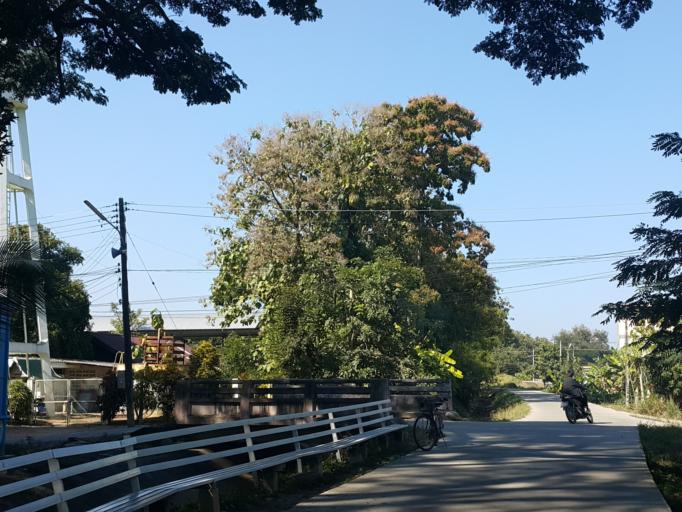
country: TH
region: Chiang Mai
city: San Sai
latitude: 18.8635
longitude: 98.9849
